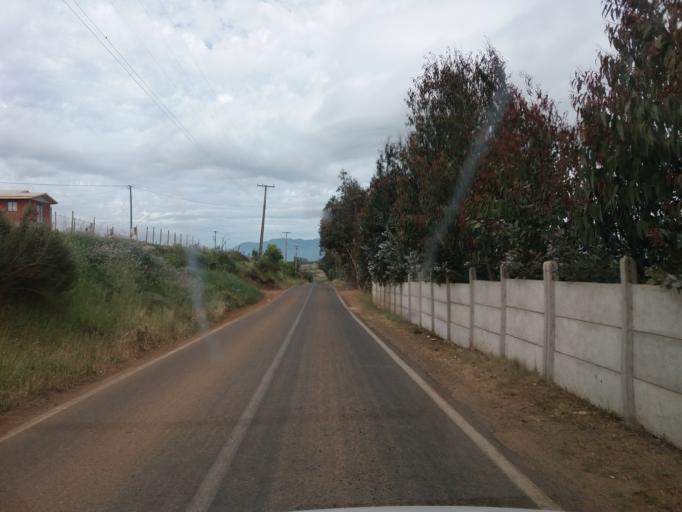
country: CL
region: Valparaiso
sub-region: Provincia de Quillota
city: Quillota
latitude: -32.9167
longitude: -71.3590
